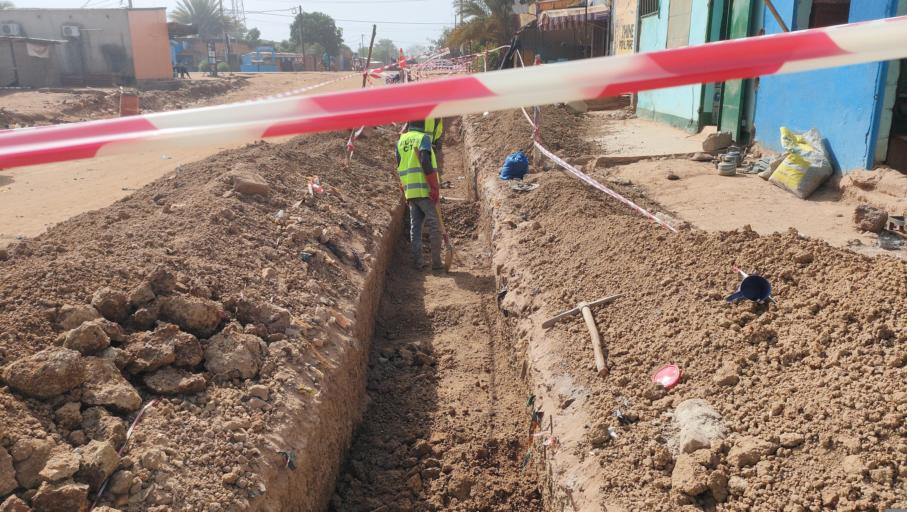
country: BF
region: Est
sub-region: Province du Gourma
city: Fada N'gourma
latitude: 12.0605
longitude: 0.3723
